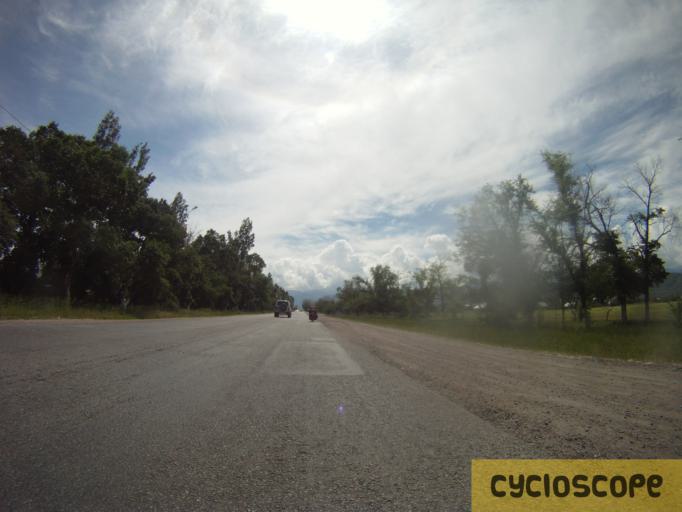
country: KZ
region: Almaty Oblysy
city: Esik
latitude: 43.3875
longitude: 77.4034
